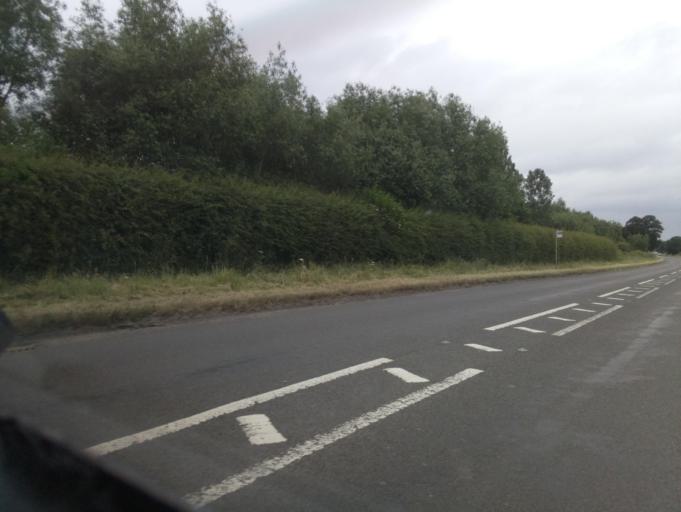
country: GB
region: England
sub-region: Staffordshire
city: Penkridge
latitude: 52.7426
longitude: -2.1084
